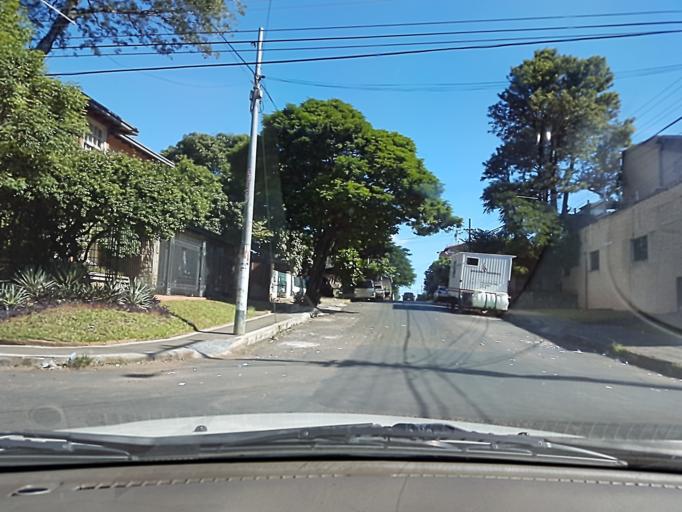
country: PY
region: Central
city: Lambare
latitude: -25.3201
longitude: -57.5909
